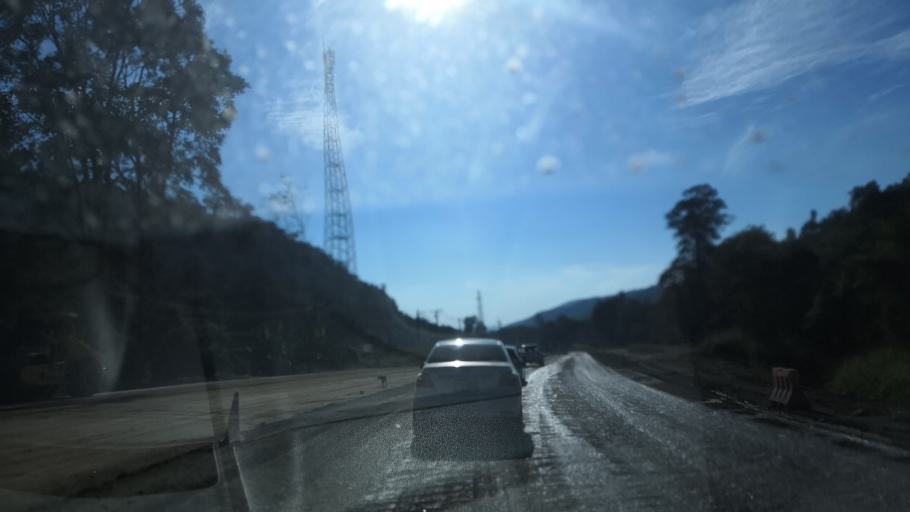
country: TH
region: Chiang Mai
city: Mae On
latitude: 19.0187
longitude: 99.3077
